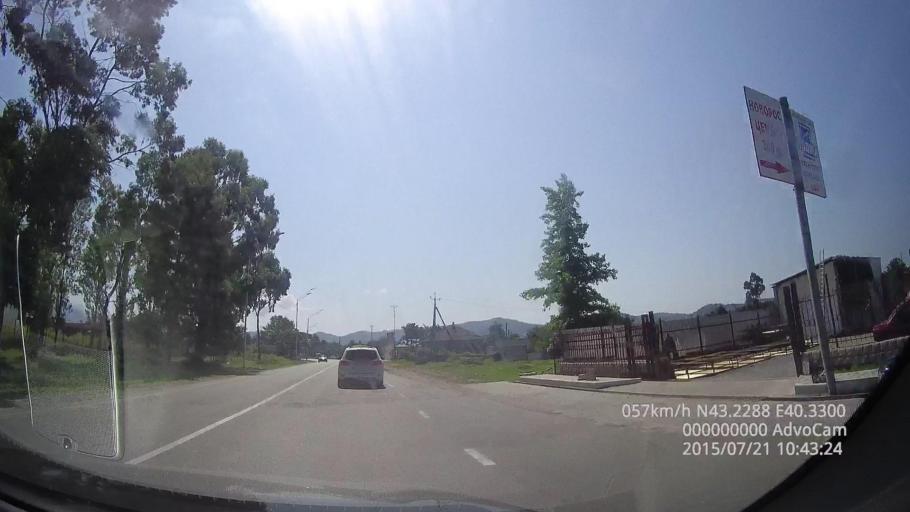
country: GE
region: Abkhazia
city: Bich'vinta
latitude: 43.2288
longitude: 40.3303
